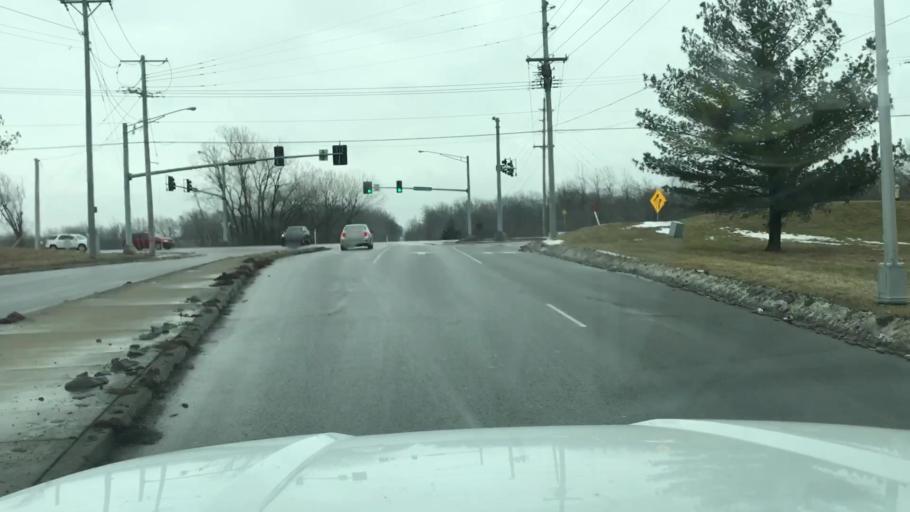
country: US
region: Missouri
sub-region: Andrew County
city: Country Club Village
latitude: 39.8070
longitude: -94.8117
